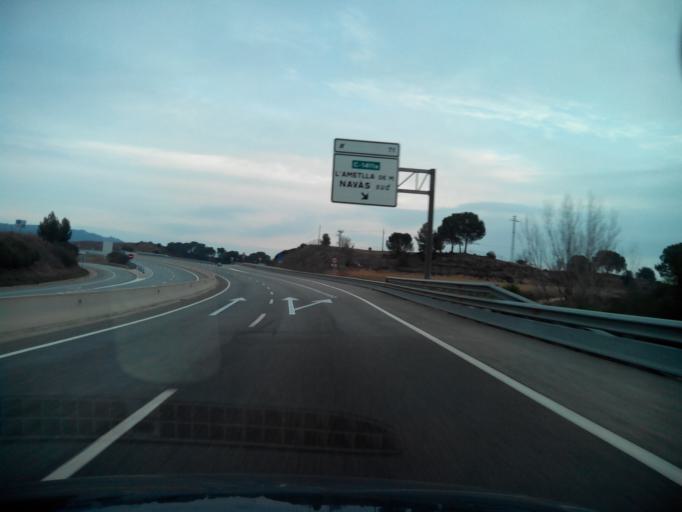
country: ES
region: Catalonia
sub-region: Provincia de Barcelona
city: Navas
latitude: 41.8853
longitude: 1.8769
